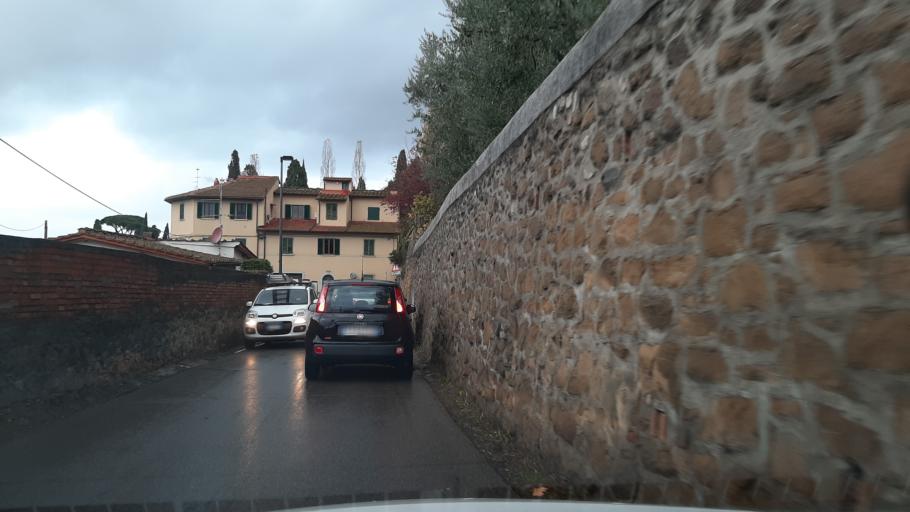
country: IT
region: Tuscany
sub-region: Province of Florence
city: Florence
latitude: 43.8102
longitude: 11.2576
